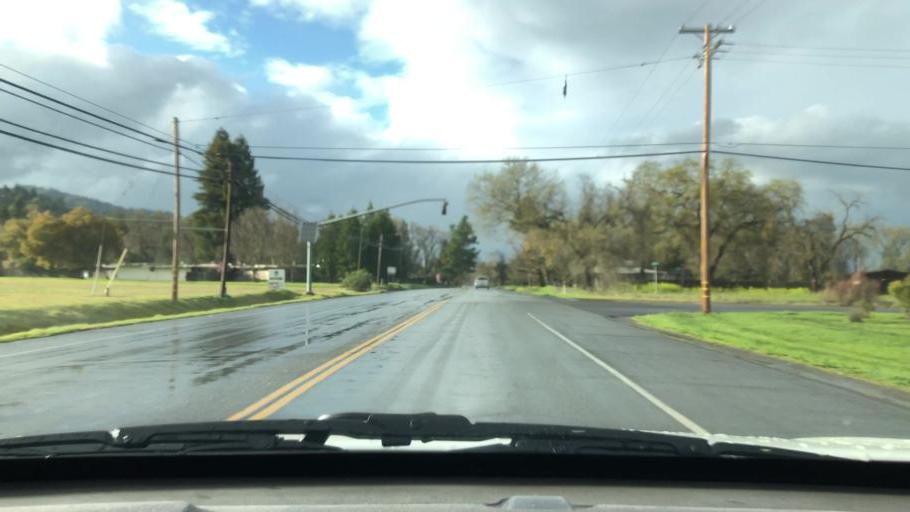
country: US
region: California
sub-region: Mendocino County
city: Talmage
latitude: 39.1115
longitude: -123.1975
